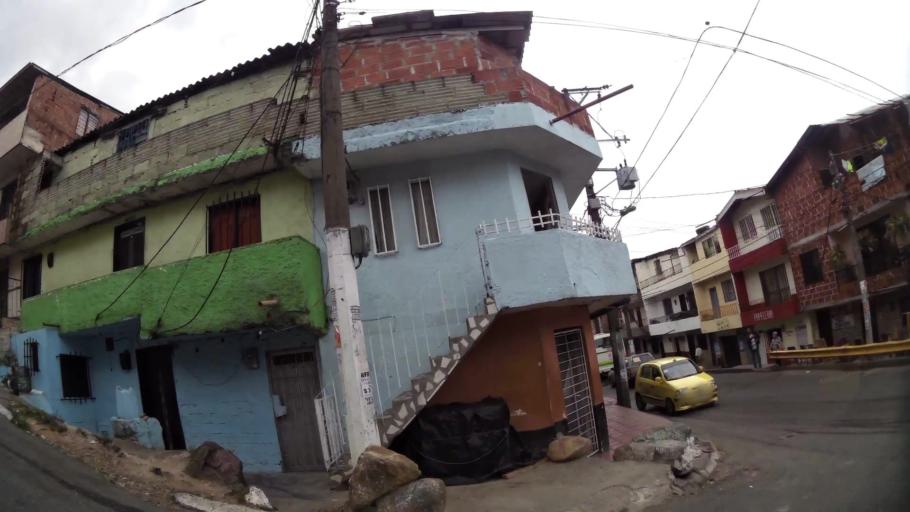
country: CO
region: Antioquia
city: Medellin
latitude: 6.2921
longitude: -75.5536
